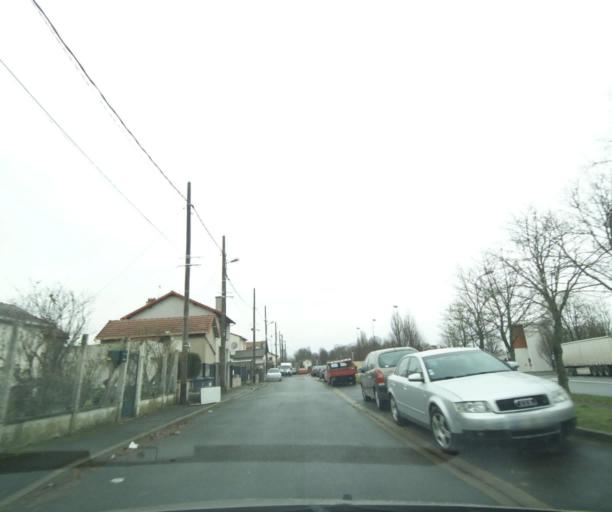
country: FR
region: Ile-de-France
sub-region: Departement du Val-de-Marne
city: Villeneuve-le-Roi
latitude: 48.7318
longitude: 2.4057
